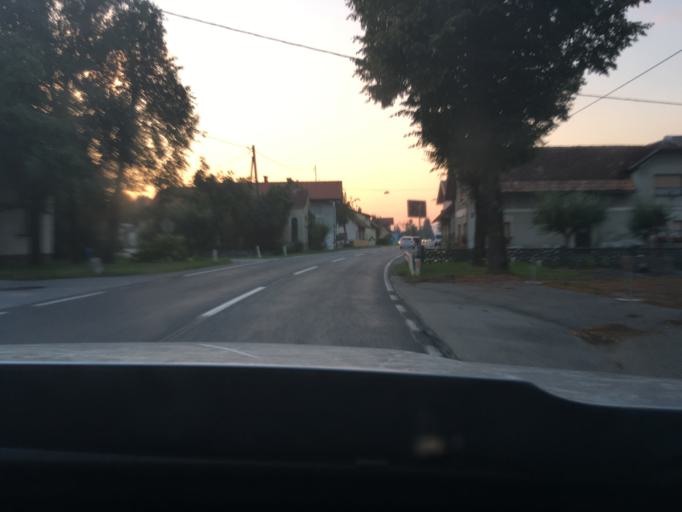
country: SI
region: Ribnica
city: Ribnica
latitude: 45.7219
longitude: 14.7425
